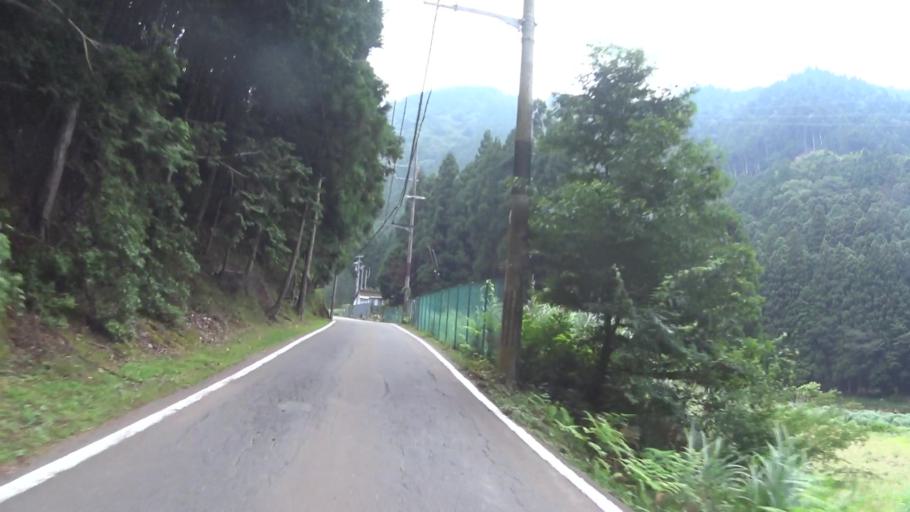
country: JP
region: Shiga Prefecture
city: Kitahama
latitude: 35.2054
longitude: 135.7592
